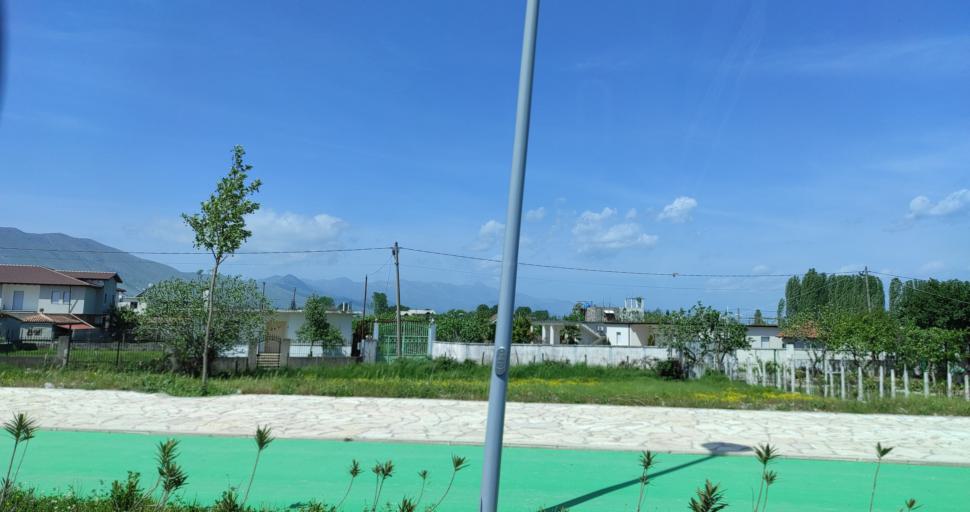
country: AL
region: Shkoder
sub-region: Rrethi i Shkodres
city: Shkoder
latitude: 42.0785
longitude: 19.4922
